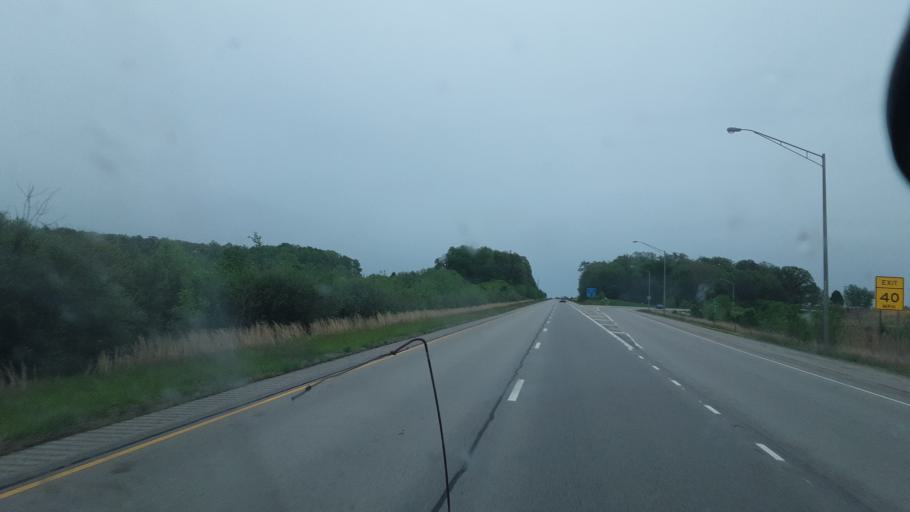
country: US
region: Indiana
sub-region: Spencer County
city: Dale
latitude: 38.1949
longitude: -86.9558
